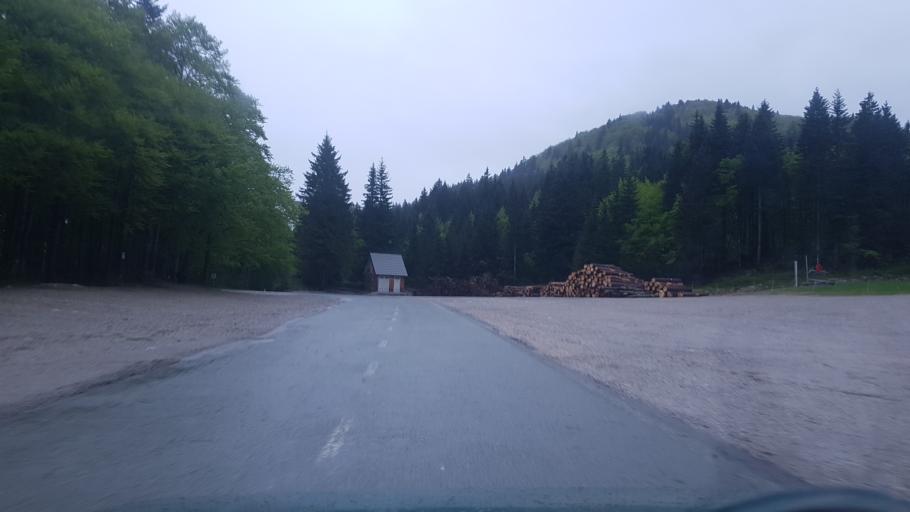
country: SI
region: Bohinj
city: Bohinjska Bistrica
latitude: 46.2412
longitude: 14.0102
